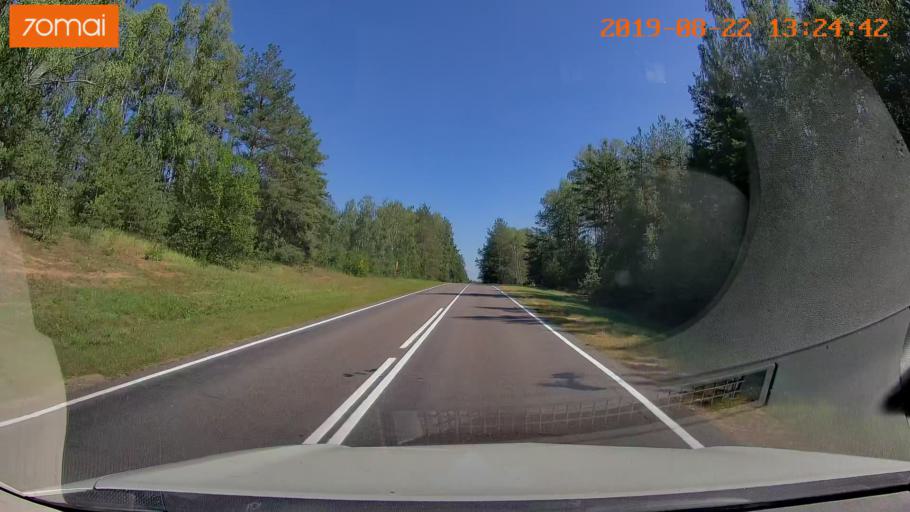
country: BY
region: Minsk
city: Staryya Darohi
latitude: 53.2112
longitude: 28.0279
